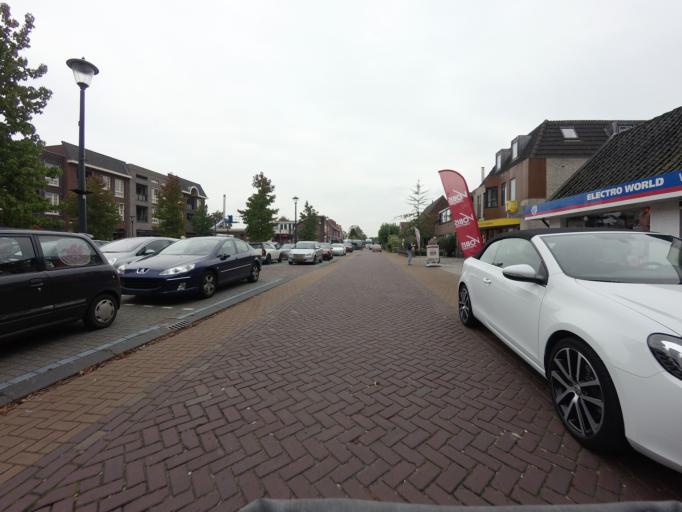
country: NL
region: North Holland
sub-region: Gemeente Wijdemeren
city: Nieuw-Loosdrecht
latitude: 52.1998
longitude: 5.1386
